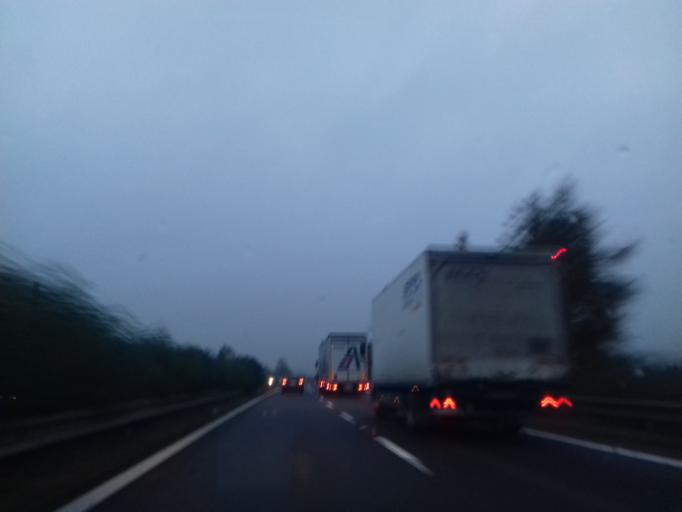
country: CZ
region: Olomoucky
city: Litovel
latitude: 49.6866
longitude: 17.0540
